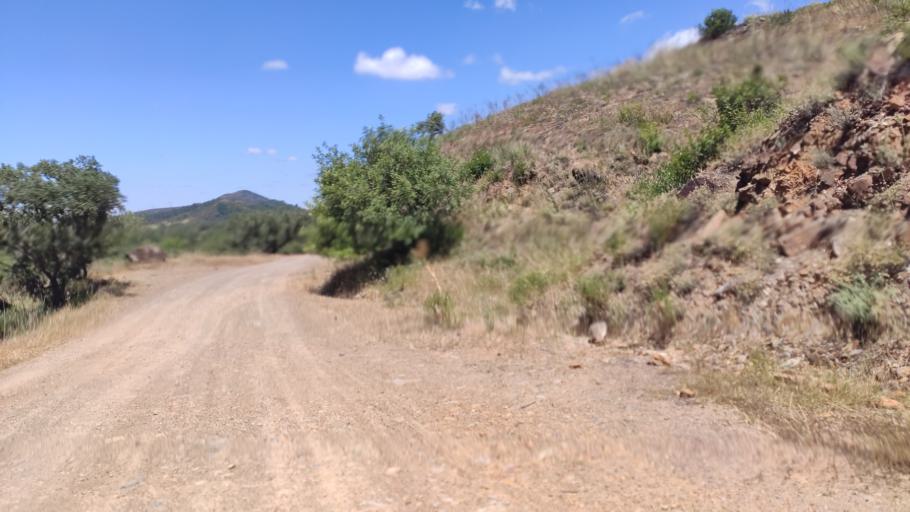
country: PT
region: Faro
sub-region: Sao Bras de Alportel
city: Sao Bras de Alportel
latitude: 37.1760
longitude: -7.9317
